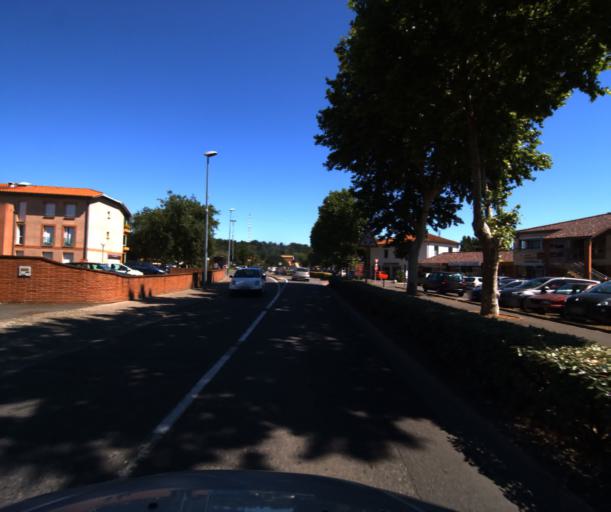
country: FR
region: Midi-Pyrenees
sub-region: Departement de la Haute-Garonne
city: Muret
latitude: 43.4564
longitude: 1.3296
